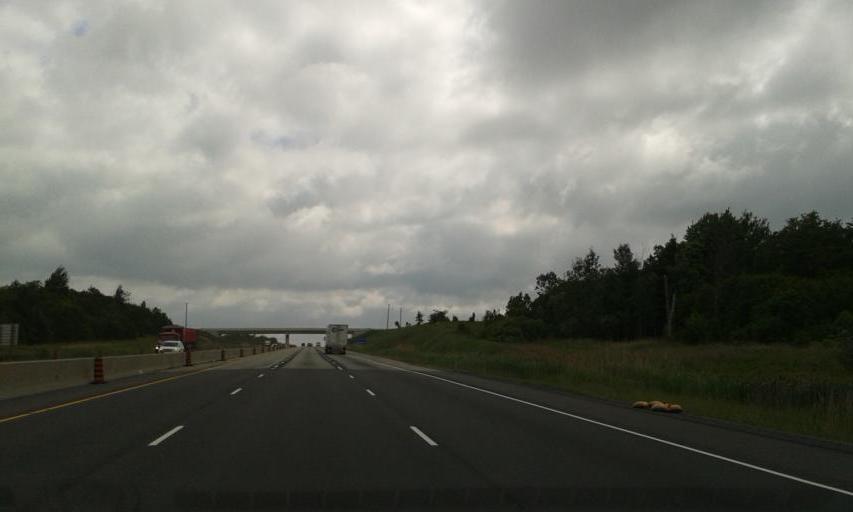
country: CA
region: Ontario
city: Cobourg
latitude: 43.9388
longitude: -78.4538
